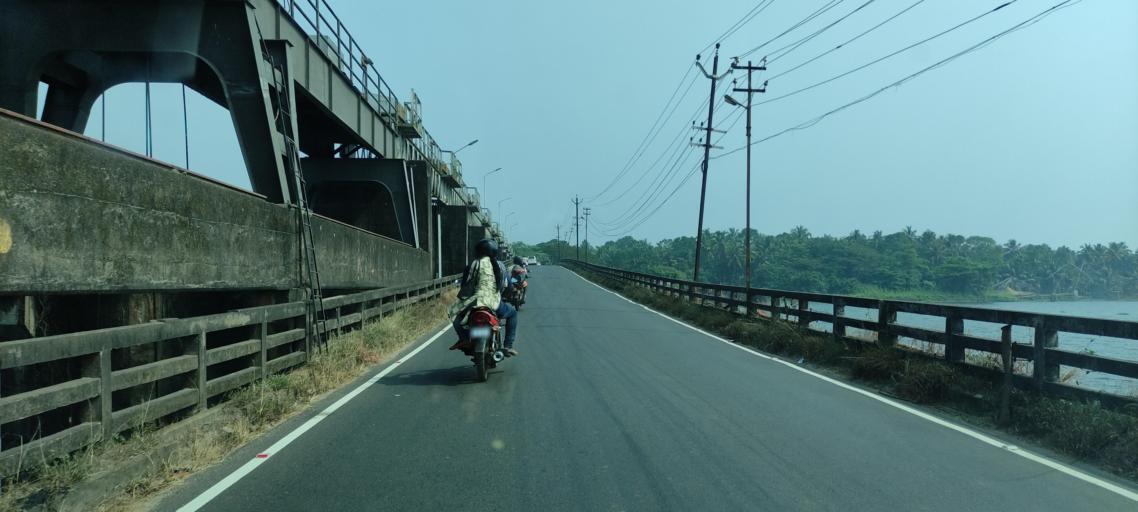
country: IN
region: Kerala
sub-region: Alappuzha
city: Shertallai
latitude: 9.6726
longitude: 76.4040
